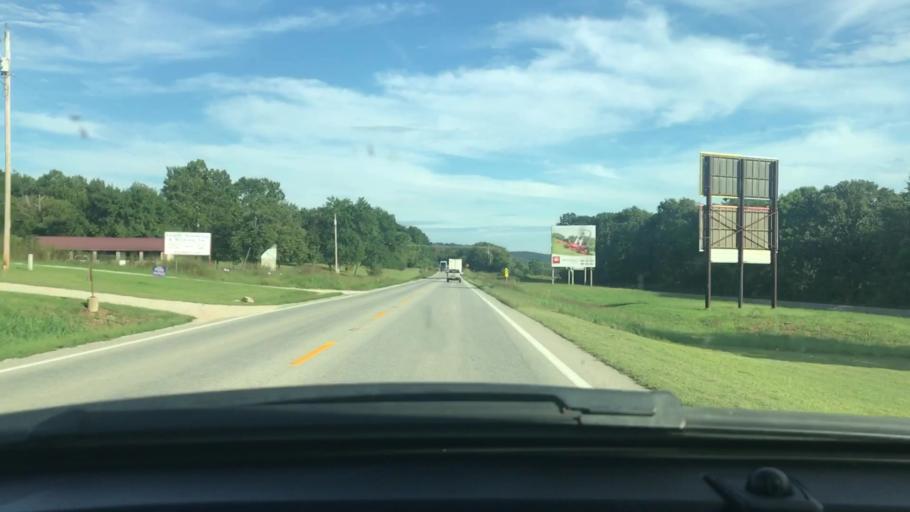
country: US
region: Arkansas
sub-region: Sharp County
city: Cherokee Village
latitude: 36.3004
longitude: -91.4418
